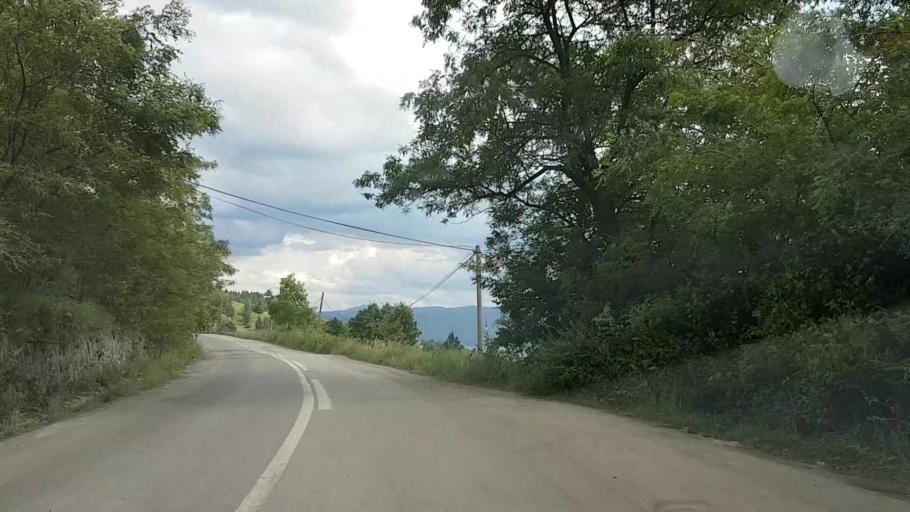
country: RO
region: Neamt
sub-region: Comuna Hangu
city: Hangu
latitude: 47.0378
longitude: 26.0593
